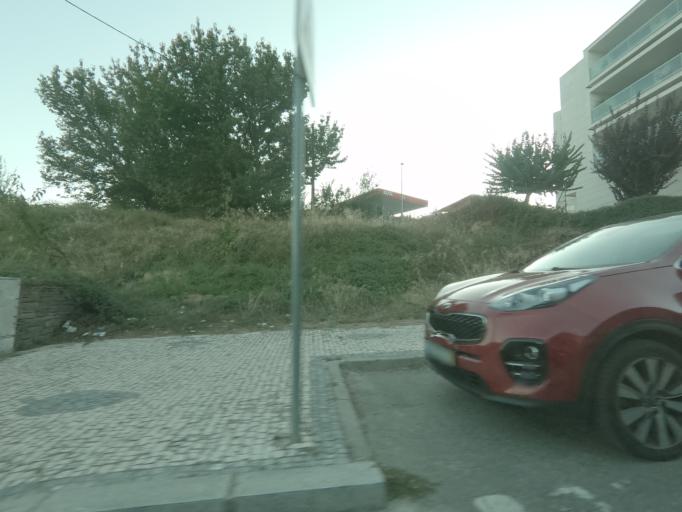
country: PT
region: Vila Real
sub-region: Peso da Regua
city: Godim
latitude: 41.1625
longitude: -7.8028
